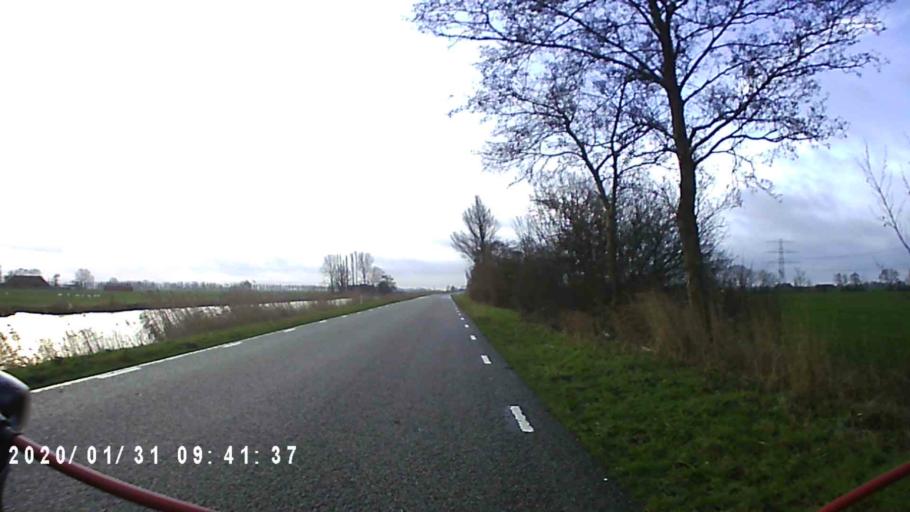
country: NL
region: Groningen
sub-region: Gemeente Zuidhorn
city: Aduard
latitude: 53.2815
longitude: 6.4846
